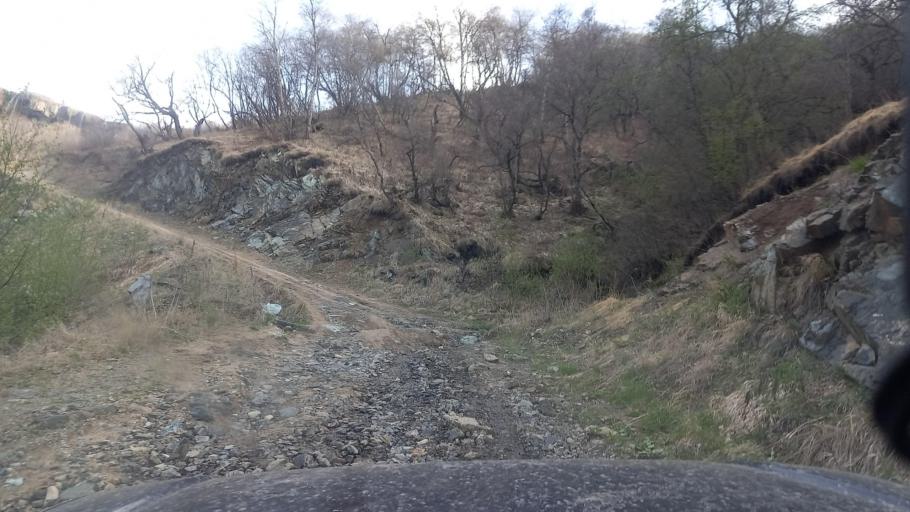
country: RU
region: Kabardino-Balkariya
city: Kamennomostskoye
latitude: 43.6928
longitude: 42.8454
